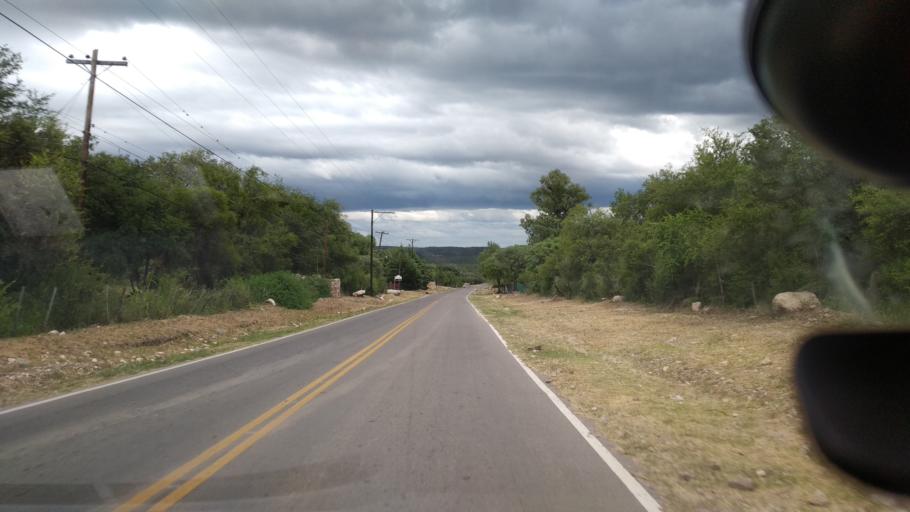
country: AR
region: Cordoba
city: Villa Las Rosas
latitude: -31.9393
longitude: -65.0344
